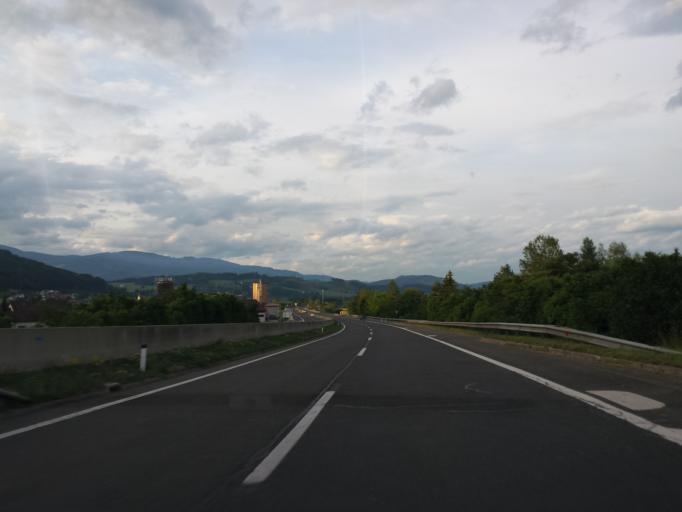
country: AT
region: Styria
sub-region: Politischer Bezirk Murtal
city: Knittelfeld
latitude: 47.2286
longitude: 14.8298
